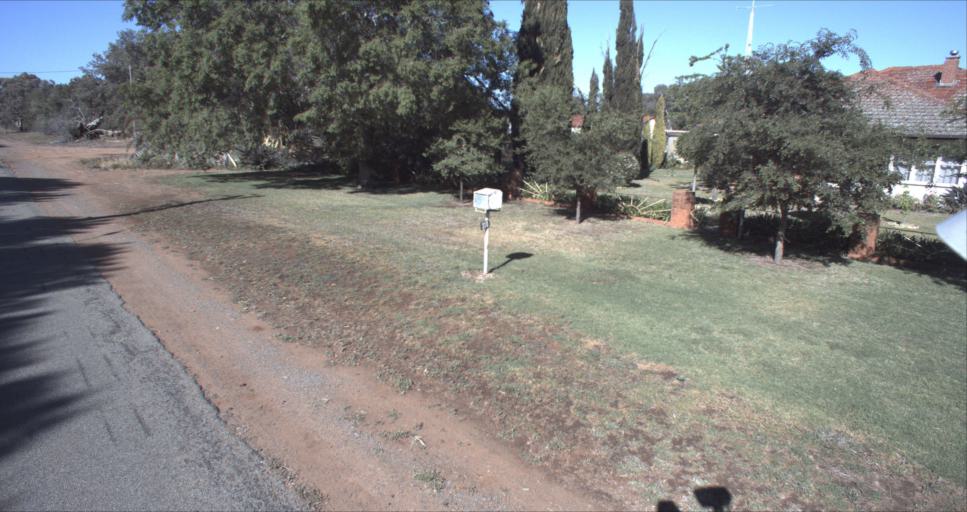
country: AU
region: New South Wales
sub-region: Leeton
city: Leeton
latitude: -34.5749
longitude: 146.3099
